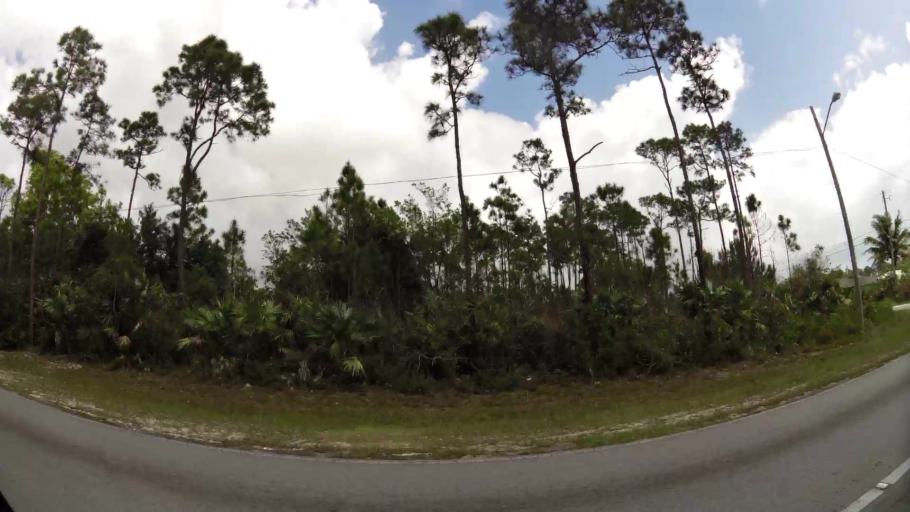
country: BS
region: Freeport
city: Lucaya
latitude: 26.5365
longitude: -78.6450
